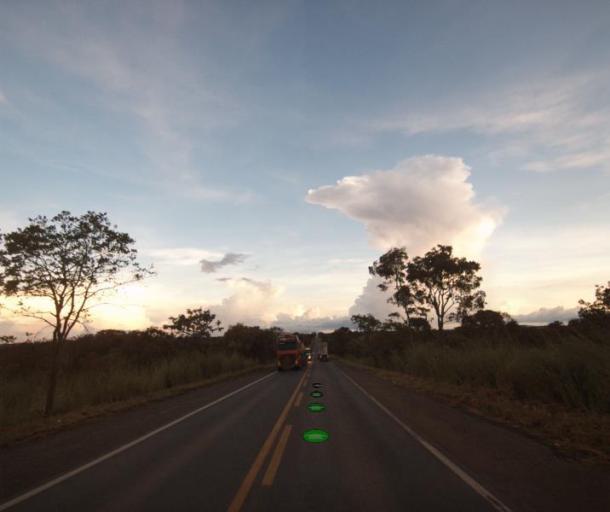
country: BR
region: Goias
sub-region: Uruacu
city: Uruacu
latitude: -14.4411
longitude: -49.1567
